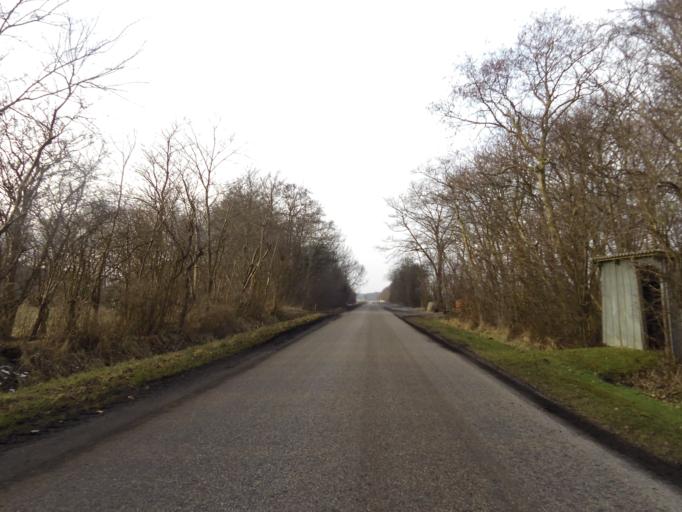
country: DK
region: South Denmark
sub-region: Tonder Kommune
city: Sherrebek
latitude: 55.1715
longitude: 8.8947
